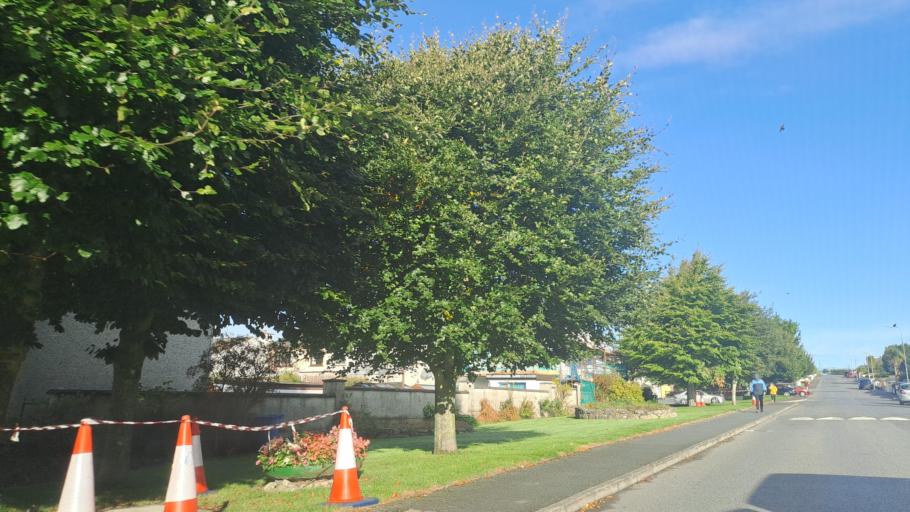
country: IE
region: Ulster
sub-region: County Monaghan
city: Carrickmacross
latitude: 53.9794
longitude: -6.7126
